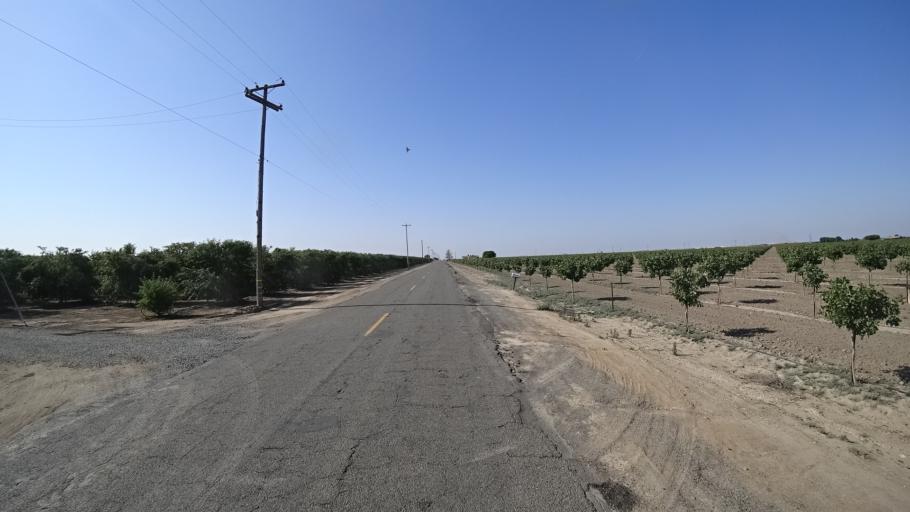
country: US
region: California
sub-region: Kings County
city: Home Garden
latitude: 36.2149
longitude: -119.5830
